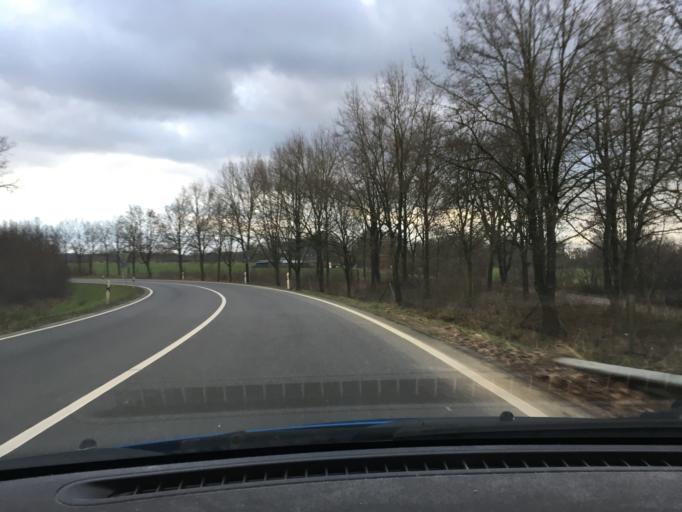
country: DE
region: Schleswig-Holstein
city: Hohenfelde
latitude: 53.8432
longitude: 9.5974
